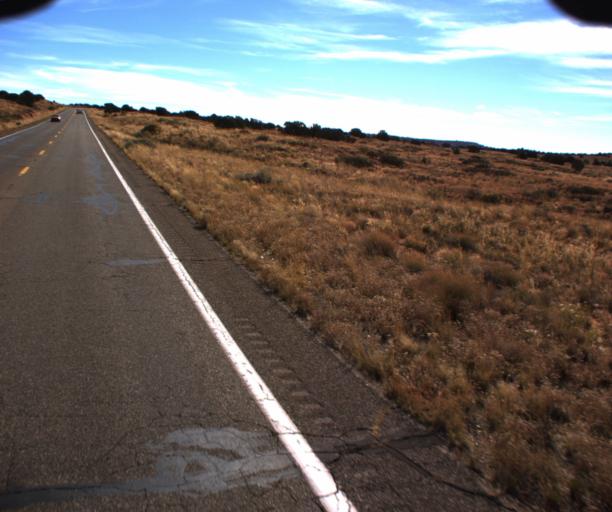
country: US
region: Arizona
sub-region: Coconino County
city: Kaibito
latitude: 36.5785
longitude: -111.1329
